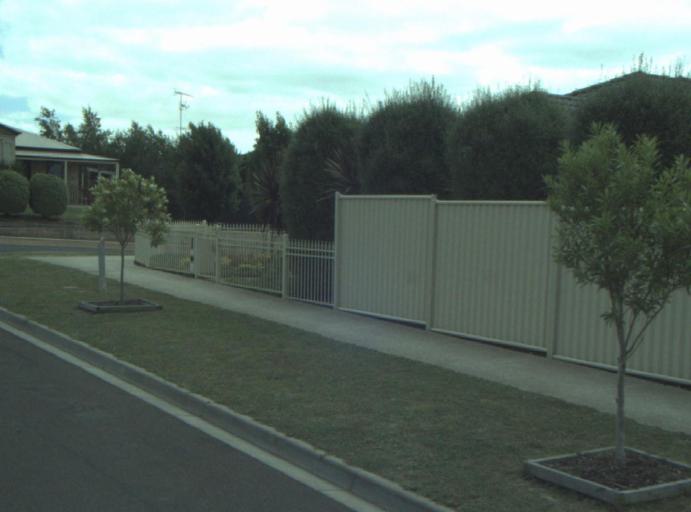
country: AU
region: Victoria
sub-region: Greater Geelong
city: Wandana Heights
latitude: -38.1958
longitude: 144.3090
